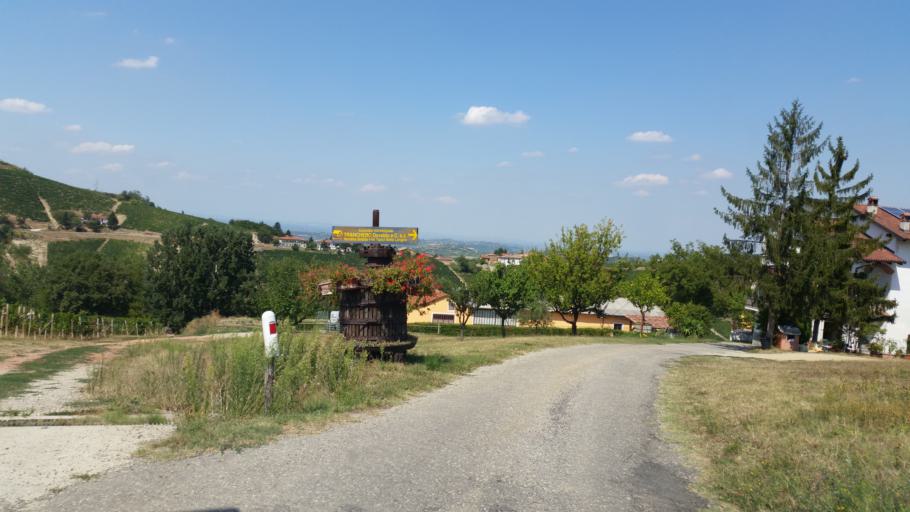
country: IT
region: Piedmont
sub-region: Provincia di Cuneo
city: Mango
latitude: 44.6917
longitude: 8.1589
